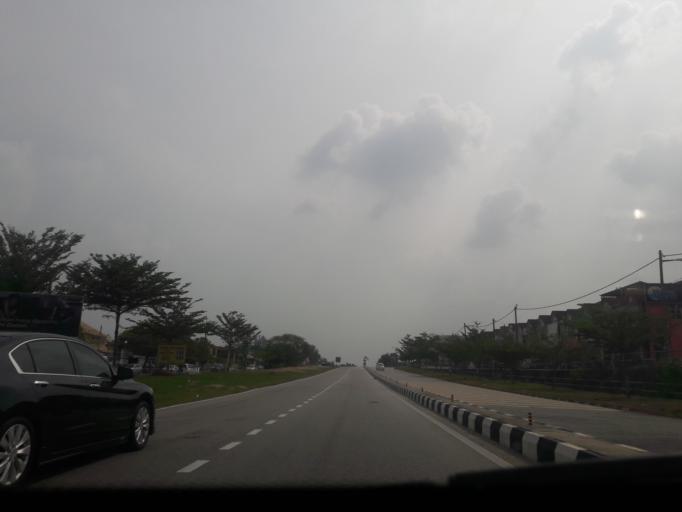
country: MY
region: Kedah
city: Kulim
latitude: 5.3694
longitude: 100.5327
